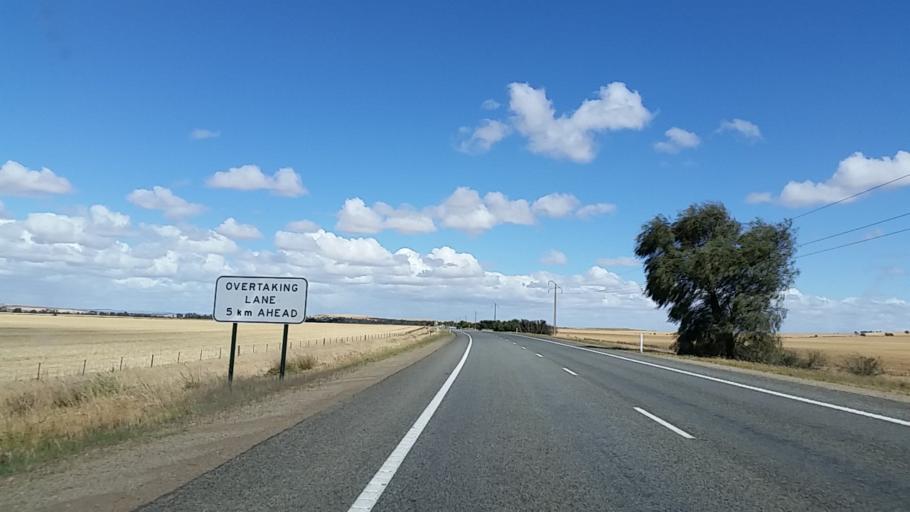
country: AU
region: South Australia
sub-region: Port Pirie City and Dists
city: Crystal Brook
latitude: -33.5180
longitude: 138.1922
